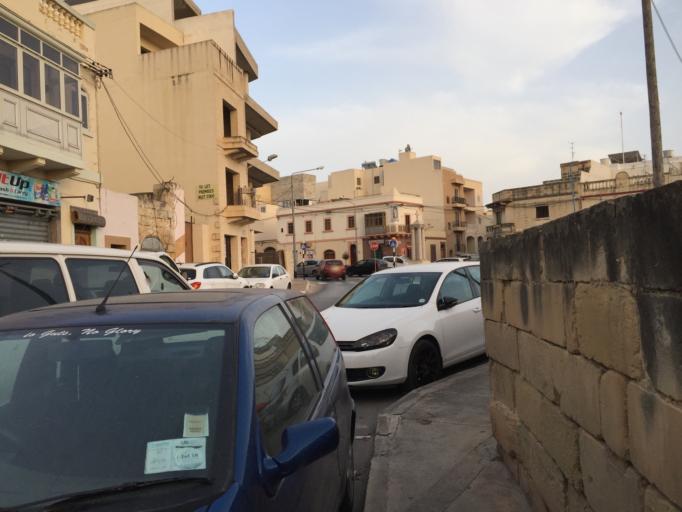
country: MT
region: Il-Fgura
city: Fgura
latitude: 35.8728
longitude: 14.5232
